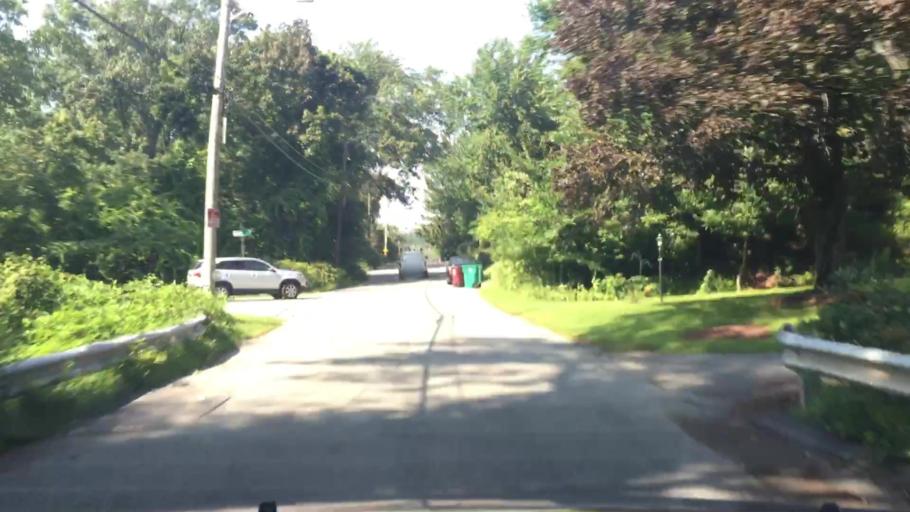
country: US
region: Massachusetts
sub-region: Middlesex County
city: Lowell
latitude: 42.6428
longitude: -71.3541
